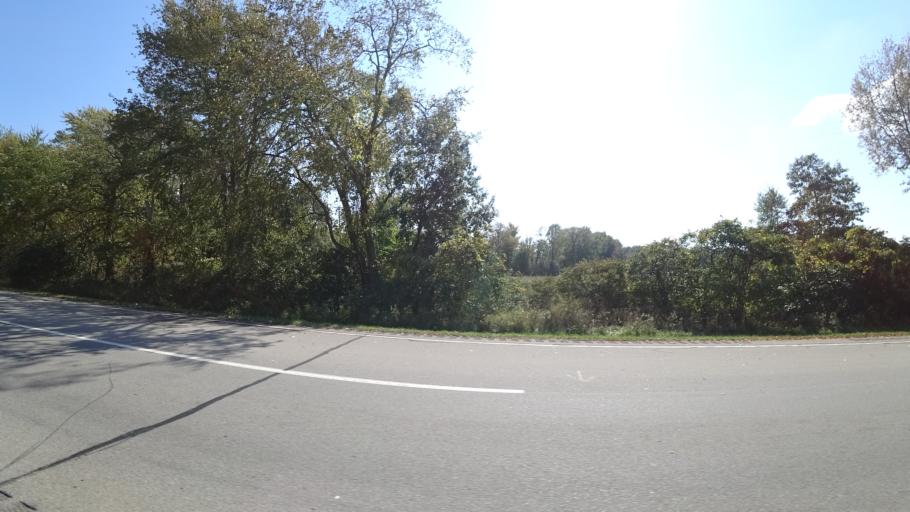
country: US
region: Michigan
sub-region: Calhoun County
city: Homer
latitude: 42.1477
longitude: -84.8191
